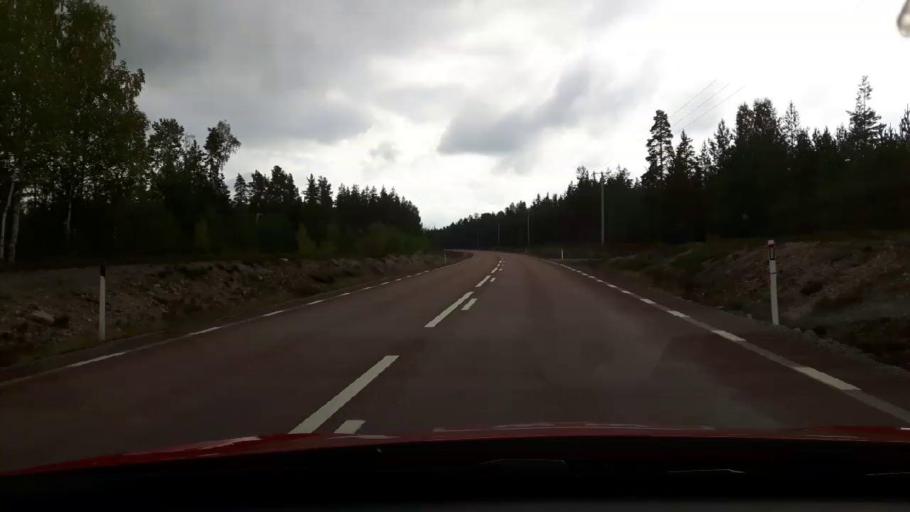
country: SE
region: Gaevleborg
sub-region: Soderhamns Kommun
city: Ljusne
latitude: 61.1117
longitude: 16.9356
